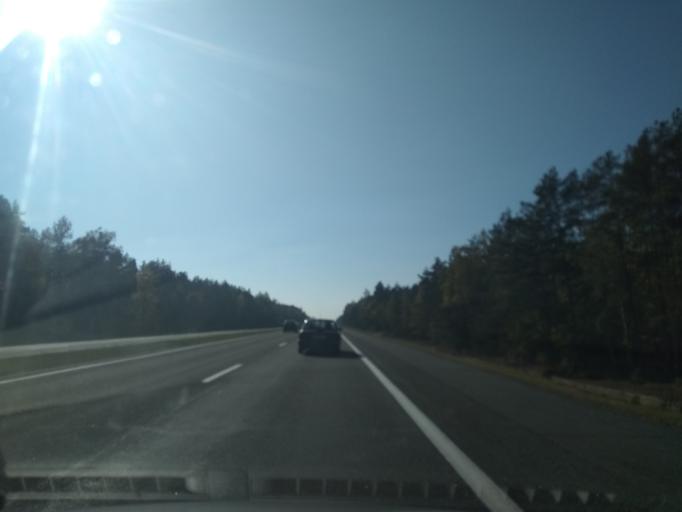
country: BY
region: Brest
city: Ivatsevichy
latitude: 52.8035
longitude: 25.5708
